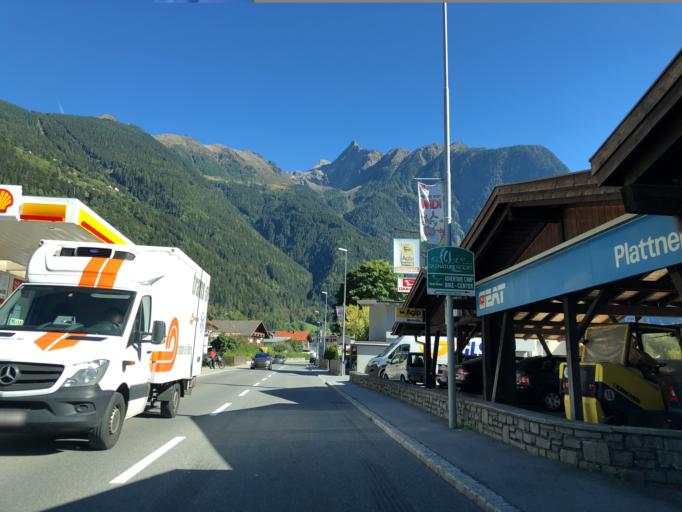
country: AT
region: Tyrol
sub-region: Politischer Bezirk Imst
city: Oetz
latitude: 47.2049
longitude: 10.8890
